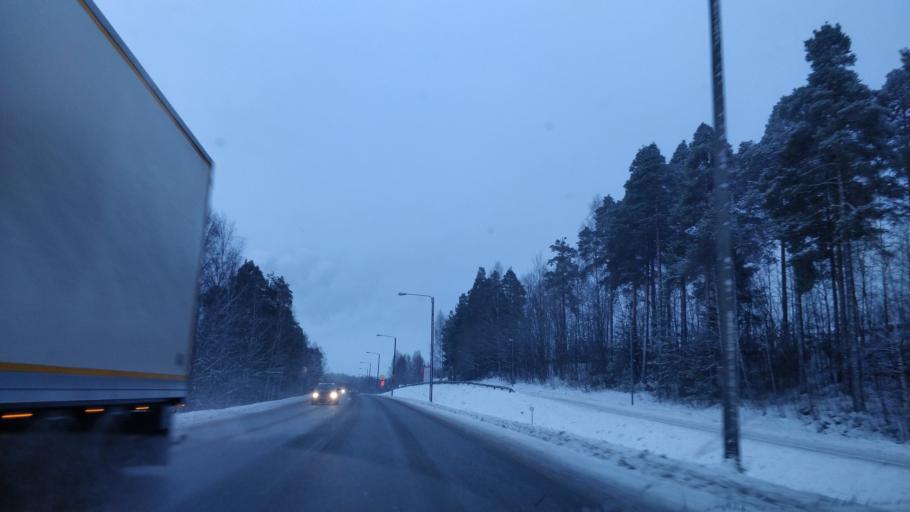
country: FI
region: Central Finland
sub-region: Saarijaervi-Viitasaari
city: Viitasaari
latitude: 63.0828
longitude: 25.8638
